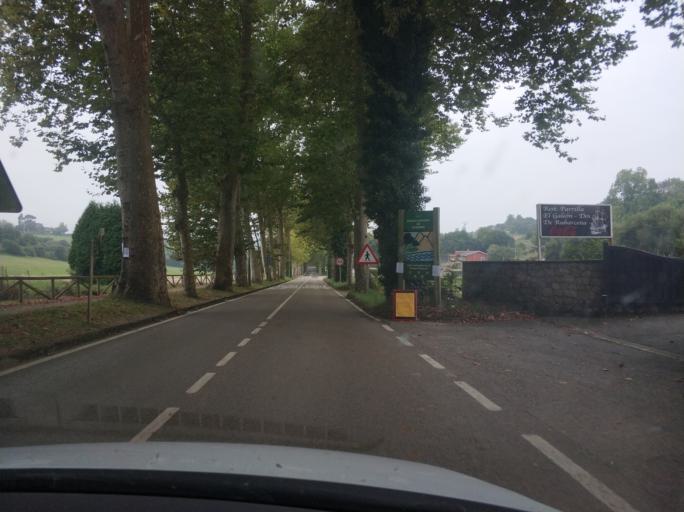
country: ES
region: Cantabria
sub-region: Provincia de Cantabria
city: Comillas
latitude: 43.3827
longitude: -4.3050
